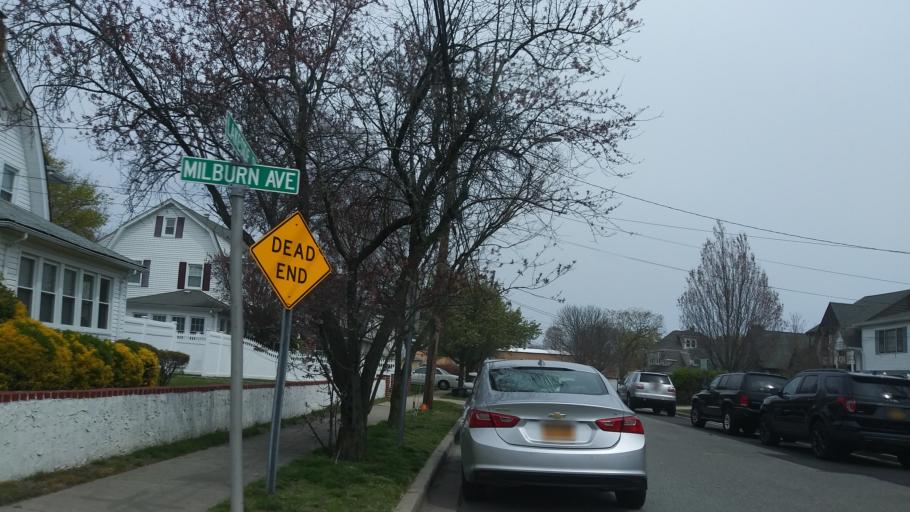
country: US
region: New York
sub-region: Nassau County
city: Baldwin
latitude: 40.6541
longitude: -73.6049
